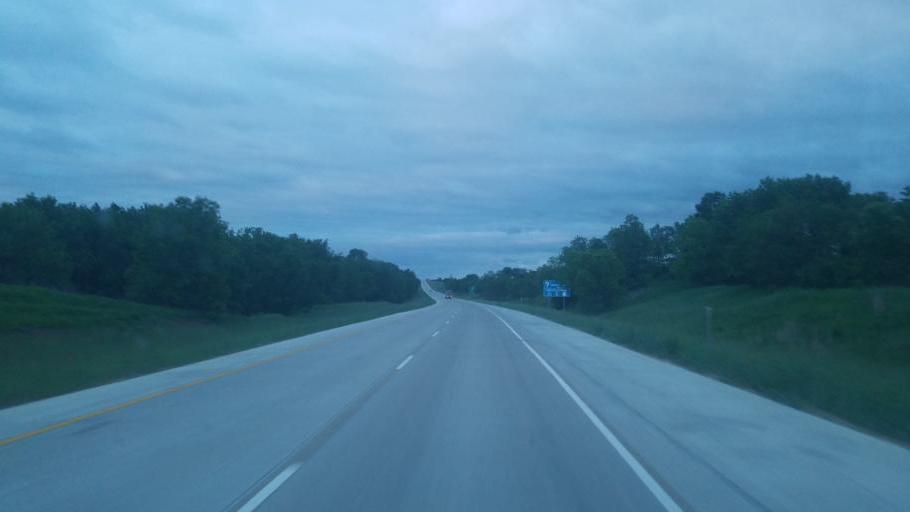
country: US
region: Iowa
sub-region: Decatur County
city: Lamoni
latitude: 40.6027
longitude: -93.9058
